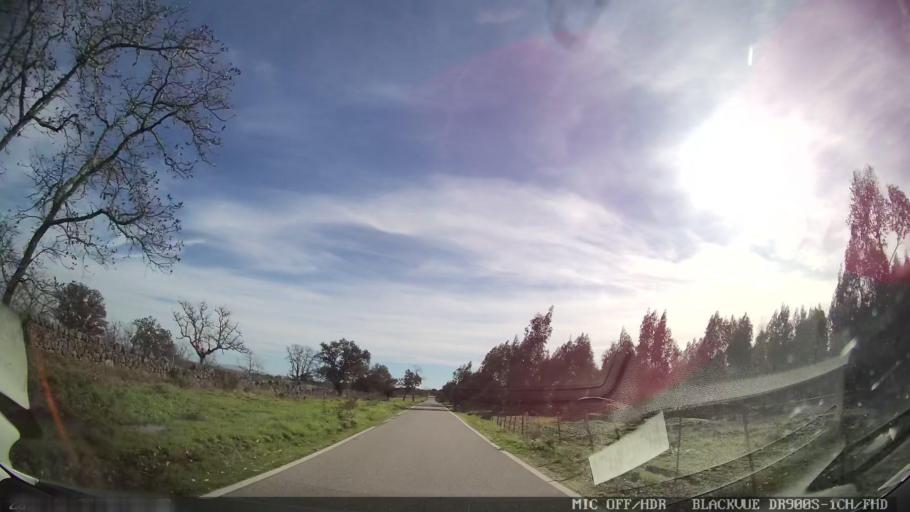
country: PT
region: Portalegre
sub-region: Nisa
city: Nisa
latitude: 39.4911
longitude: -7.7429
